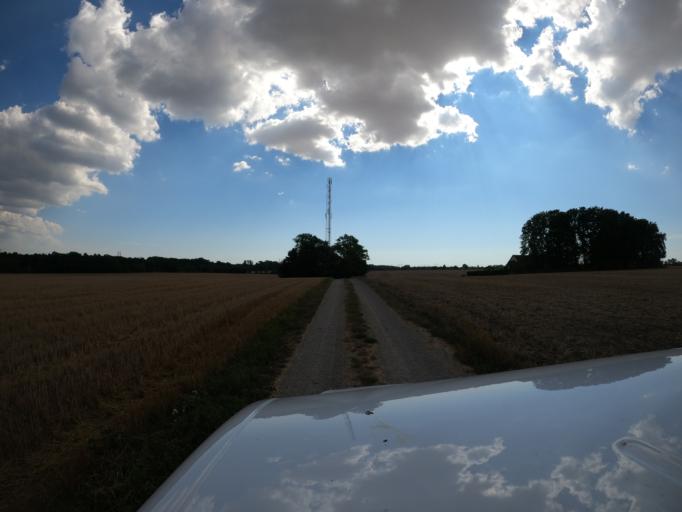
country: SE
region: Skane
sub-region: Lunds Kommun
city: Lund
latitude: 55.7093
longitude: 13.3195
